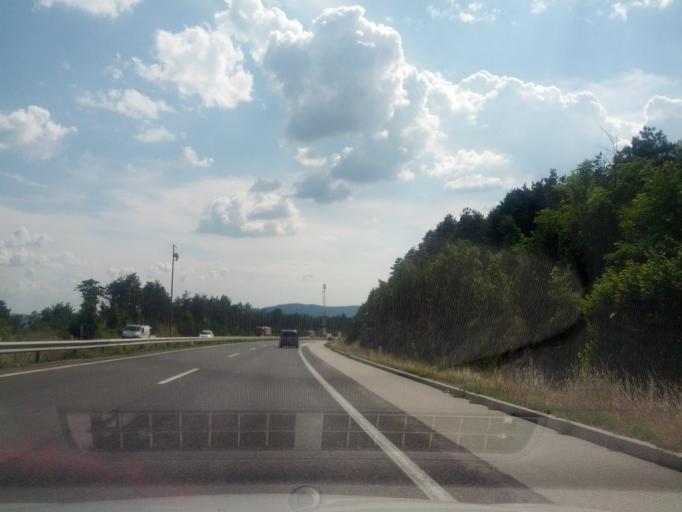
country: SI
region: Divaca
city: Divaca
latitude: 45.7048
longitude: 13.9994
